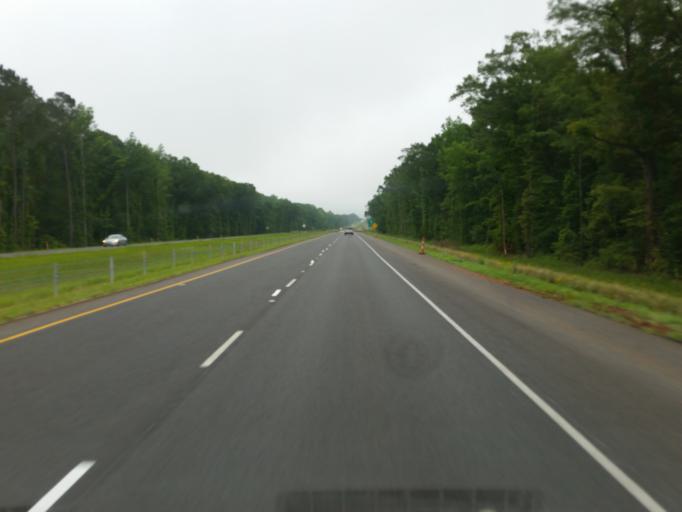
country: US
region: Louisiana
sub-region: Bienville Parish
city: Arcadia
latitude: 32.5631
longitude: -93.0947
